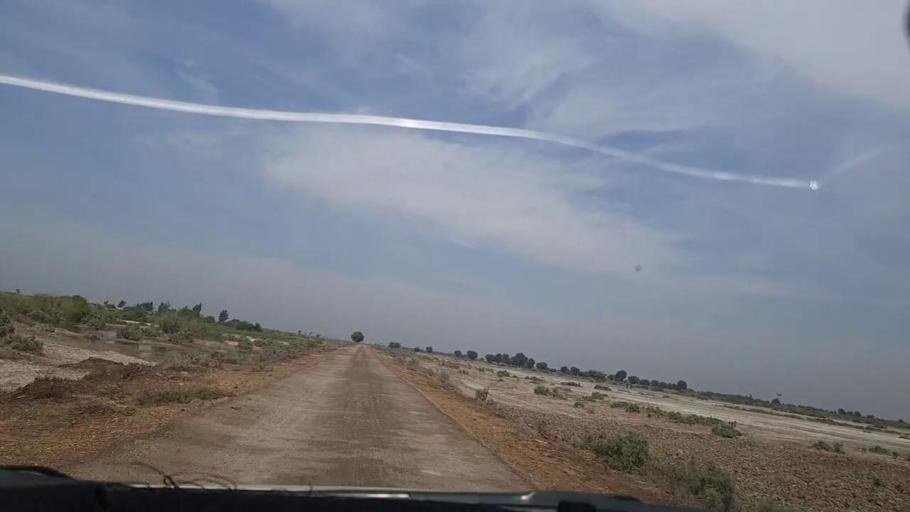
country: PK
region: Sindh
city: Pithoro
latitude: 25.4513
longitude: 69.4643
